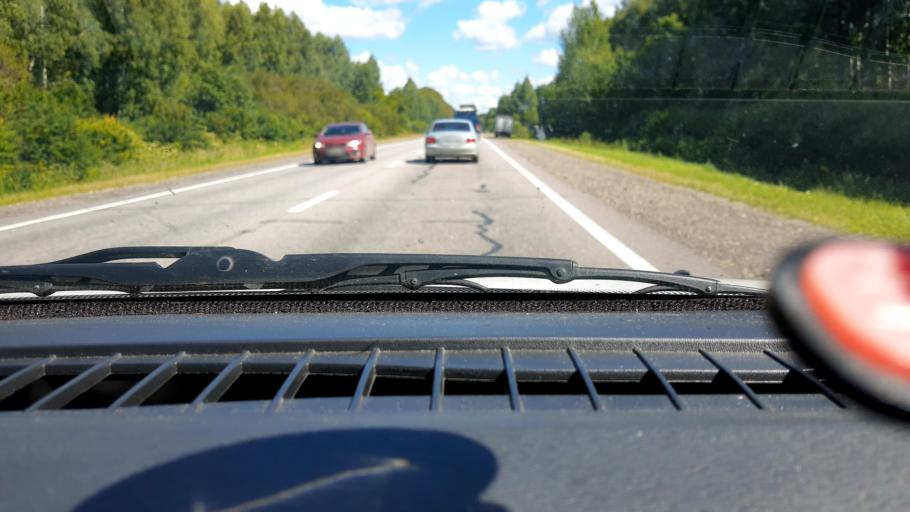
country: RU
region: Nizjnij Novgorod
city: Chernukha
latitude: 55.5620
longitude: 43.9536
